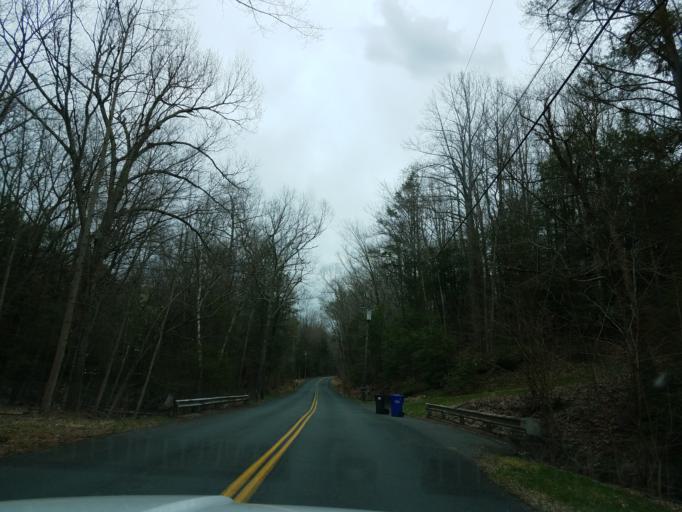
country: US
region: Connecticut
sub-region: Tolland County
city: Somers
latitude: 41.9794
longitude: -72.4208
